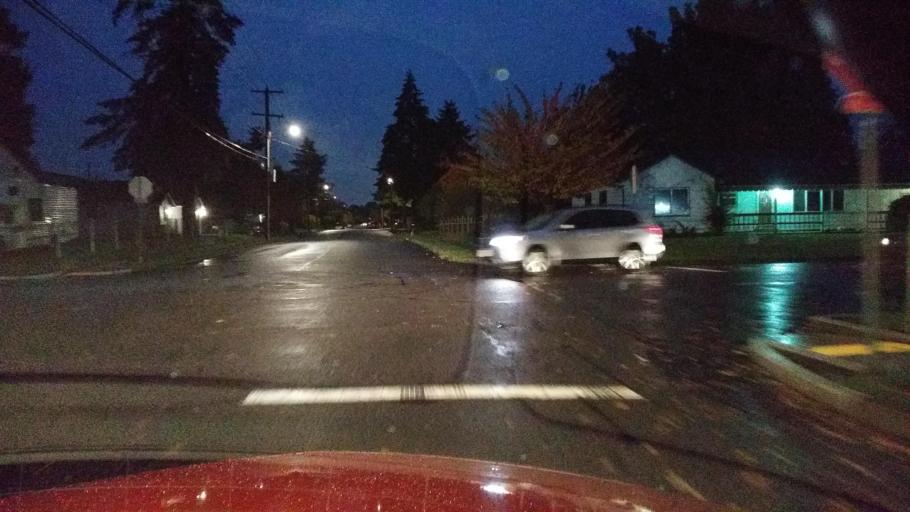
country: US
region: Oregon
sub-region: Washington County
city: Forest Grove
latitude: 45.5224
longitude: -123.0930
